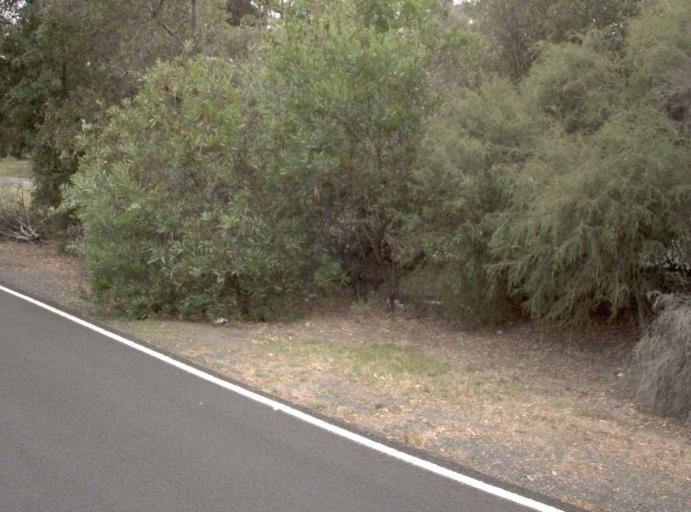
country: AU
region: Victoria
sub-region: Mornington Peninsula
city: Mount Eliza
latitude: -38.1855
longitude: 145.0968
